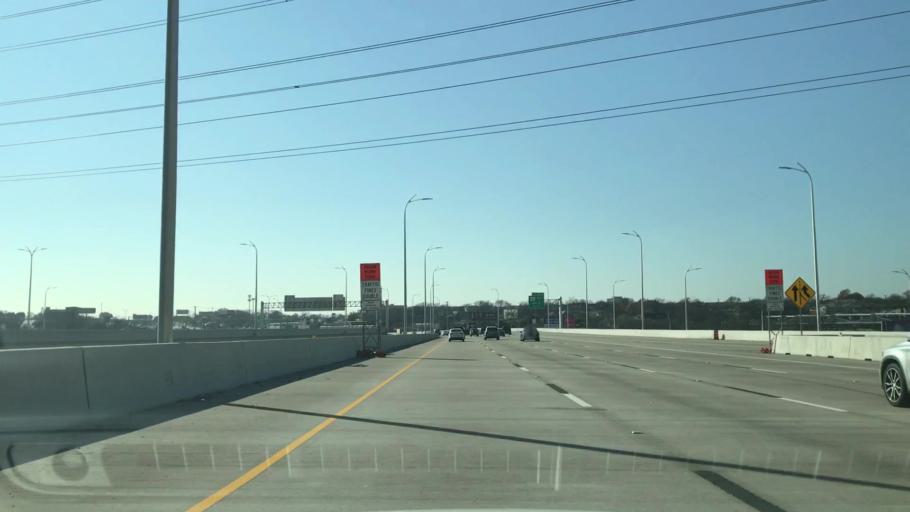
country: US
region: Texas
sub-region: Dallas County
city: Dallas
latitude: 32.7609
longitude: -96.8086
